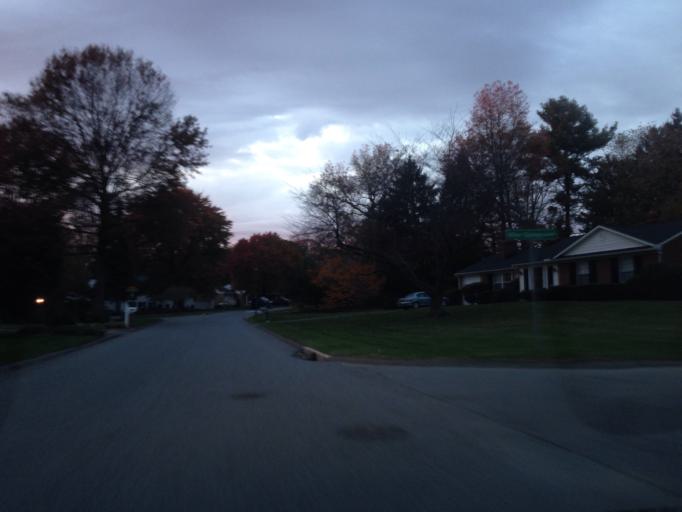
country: US
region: Maryland
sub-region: Baltimore County
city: Lutherville
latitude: 39.4097
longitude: -76.6327
